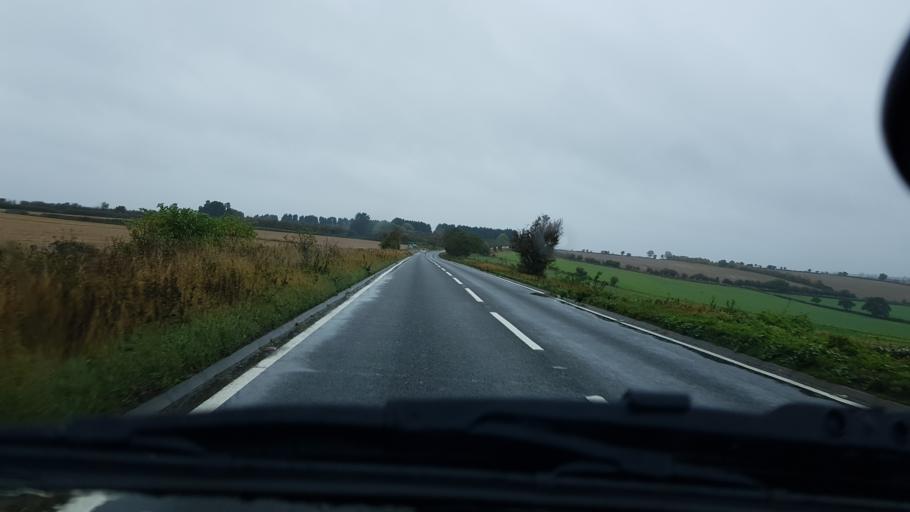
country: GB
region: England
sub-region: Oxfordshire
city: Carterton
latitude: 51.7910
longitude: -1.5920
